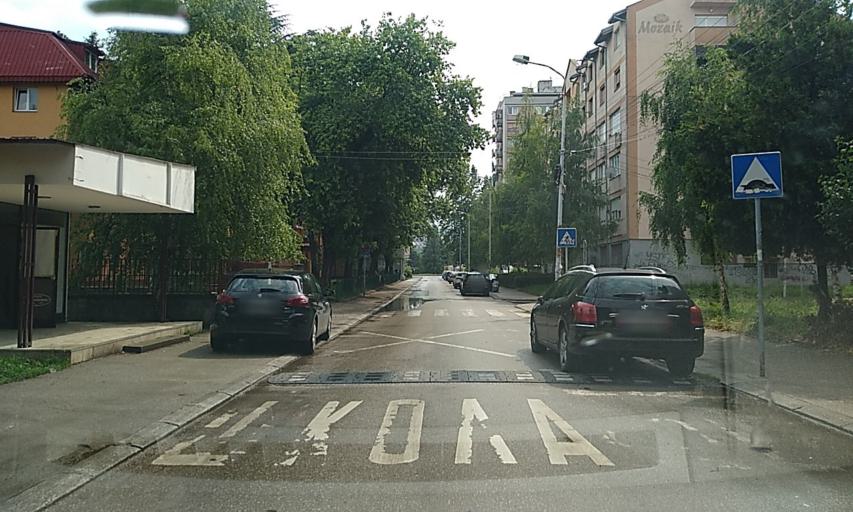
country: RS
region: Central Serbia
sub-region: Nisavski Okrug
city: Nis
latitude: 43.3175
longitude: 21.9156
